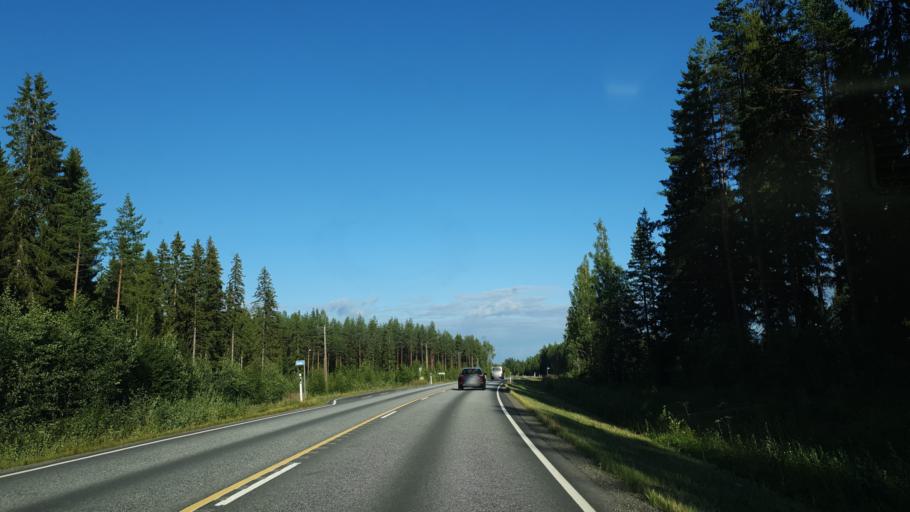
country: FI
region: North Karelia
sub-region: Joensuu
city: Outokumpu
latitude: 62.5347
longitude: 28.9490
